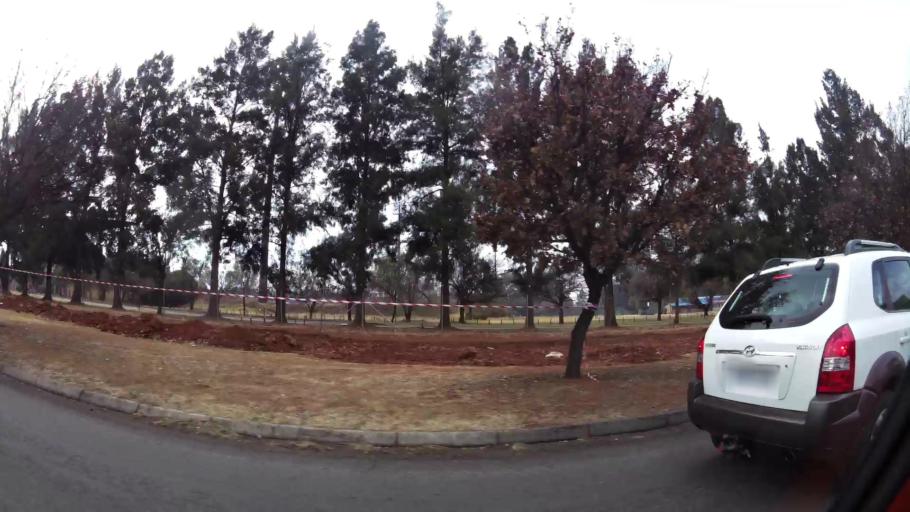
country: ZA
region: Gauteng
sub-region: Sedibeng District Municipality
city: Vanderbijlpark
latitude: -26.7062
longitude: 27.8596
